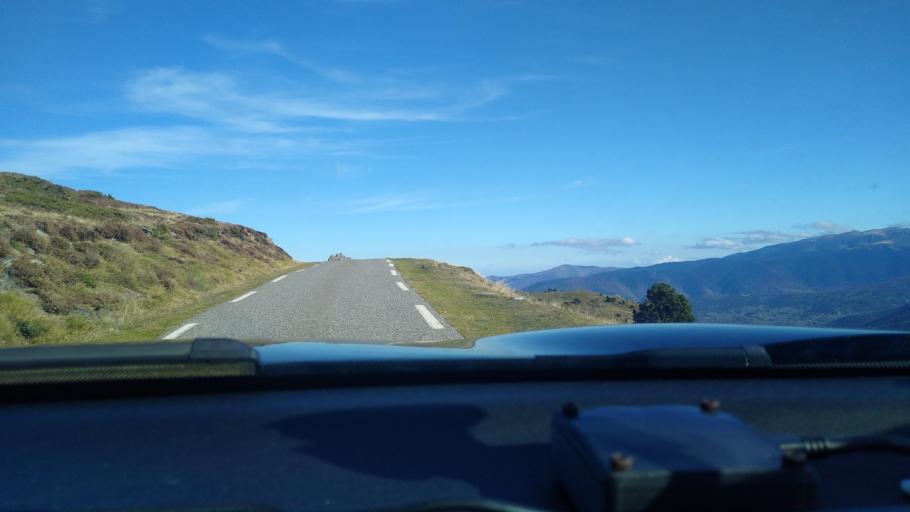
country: FR
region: Midi-Pyrenees
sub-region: Departement de l'Ariege
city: Ax-les-Thermes
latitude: 42.7352
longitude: 1.9975
